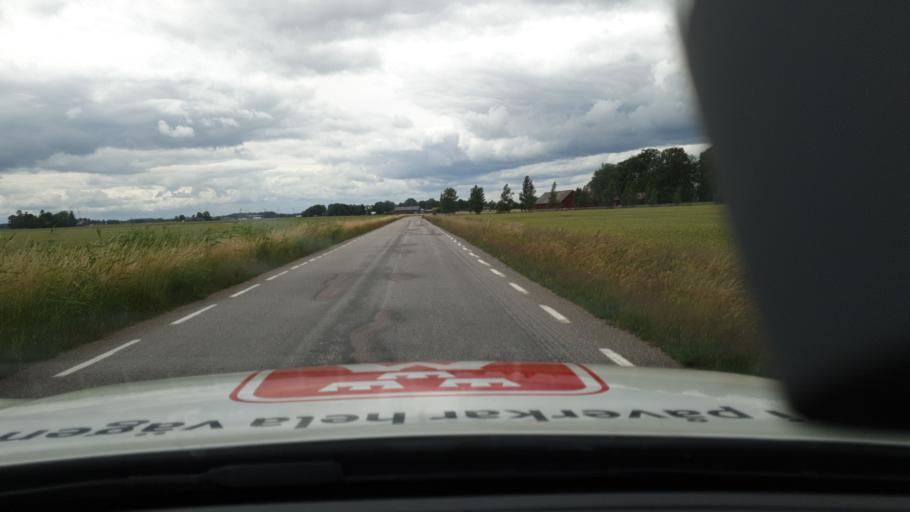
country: SE
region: Vaestra Goetaland
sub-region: Lidkopings Kommun
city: Vinninga
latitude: 58.3828
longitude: 13.3009
